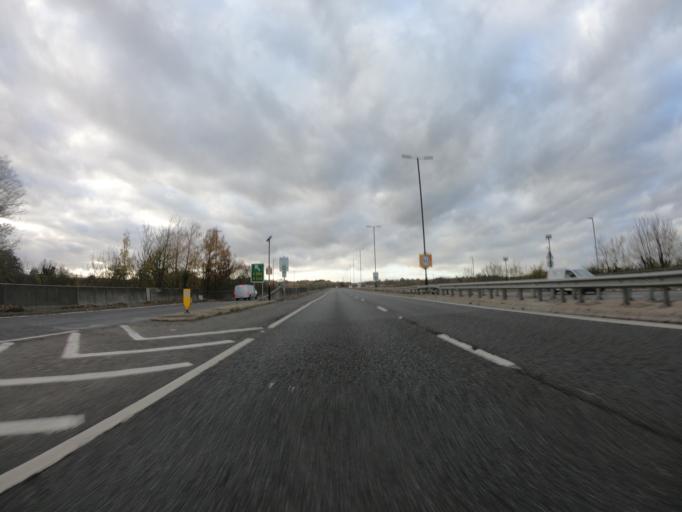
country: GB
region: England
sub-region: Greater London
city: Sidcup
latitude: 51.4121
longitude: 0.1175
